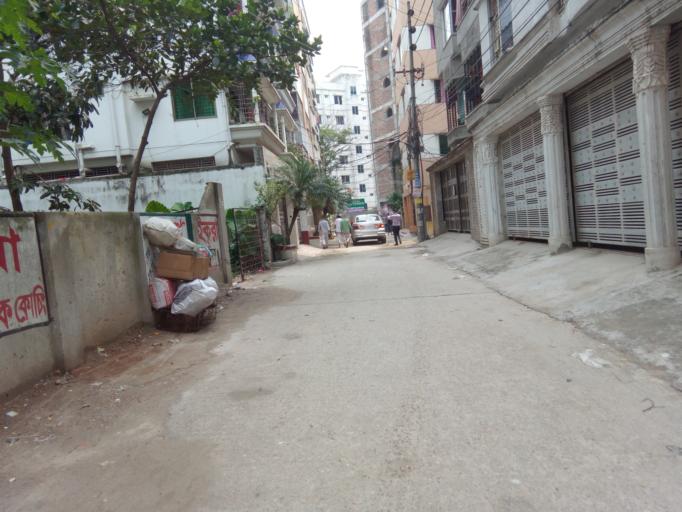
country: BD
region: Dhaka
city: Paltan
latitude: 23.7660
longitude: 90.4249
